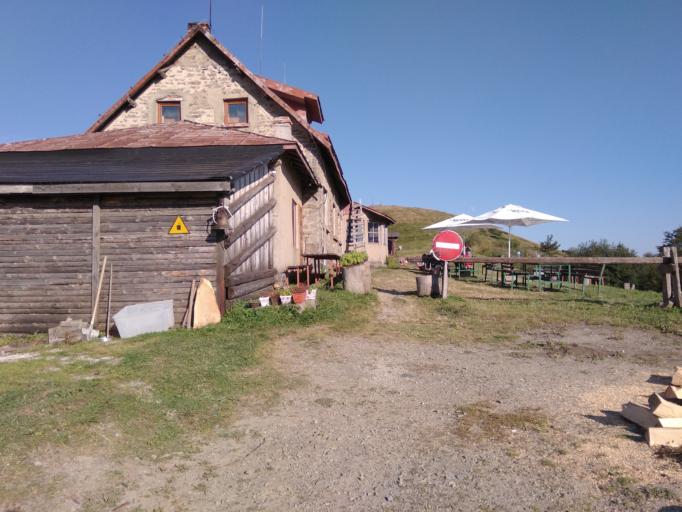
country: BG
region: Stara Zagora
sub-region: Obshtina Pavel Banya
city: Asen
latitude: 42.7587
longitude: 25.1143
